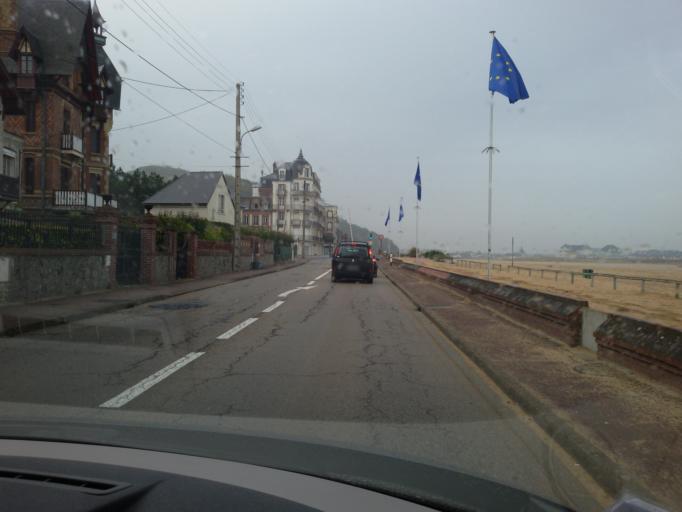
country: FR
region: Lower Normandy
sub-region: Departement du Calvados
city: Houlgate
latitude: 49.3006
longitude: -0.0831
